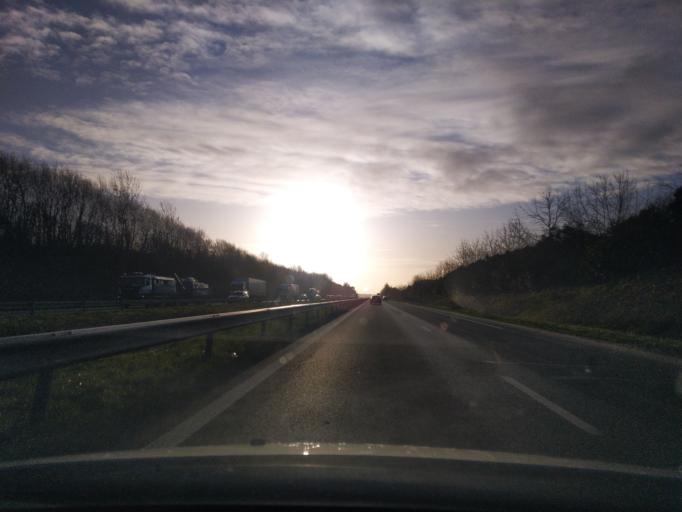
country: FR
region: Haute-Normandie
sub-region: Departement de la Seine-Maritime
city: Maromme
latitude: 49.4783
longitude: 1.0160
